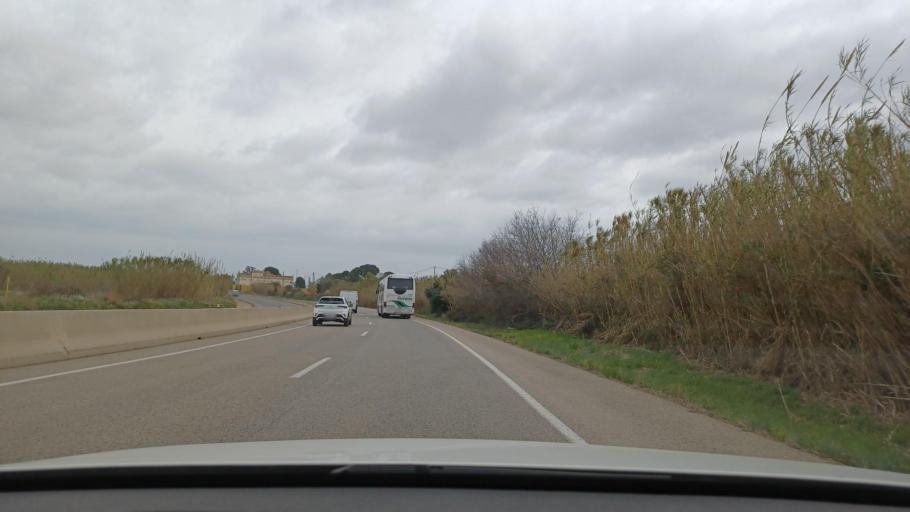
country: ES
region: Catalonia
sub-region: Provincia de Tarragona
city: Vila-seca
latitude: 41.1307
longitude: 1.1465
